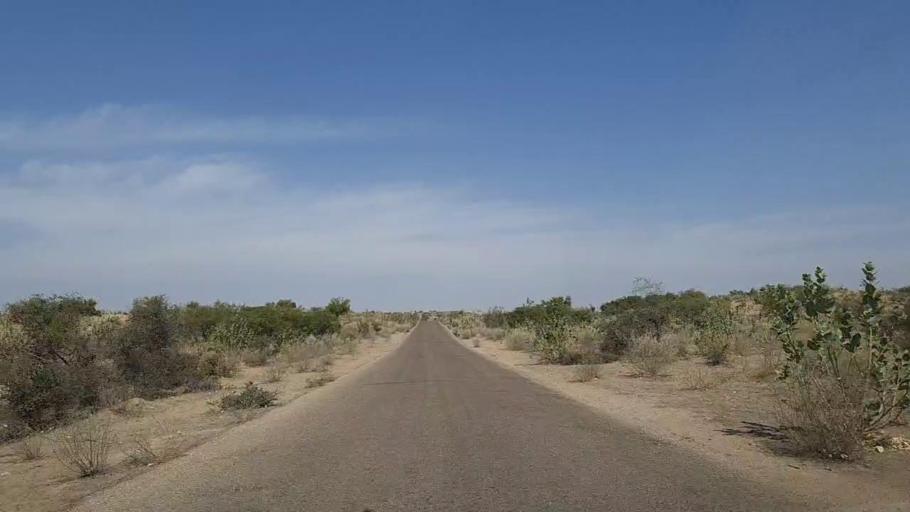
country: PK
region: Sindh
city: Nabisar
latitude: 25.1047
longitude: 69.9950
